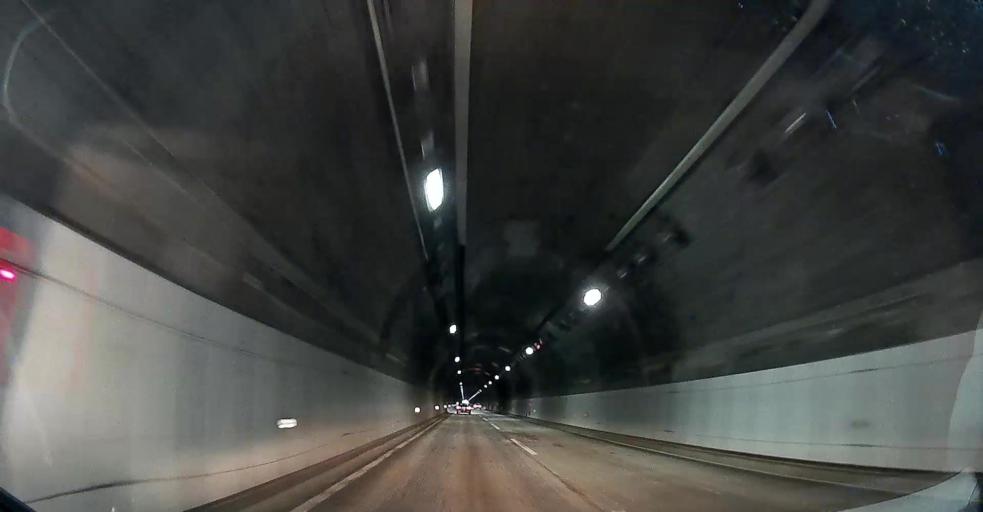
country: JP
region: Kanagawa
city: Odawara
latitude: 35.2495
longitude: 139.1330
